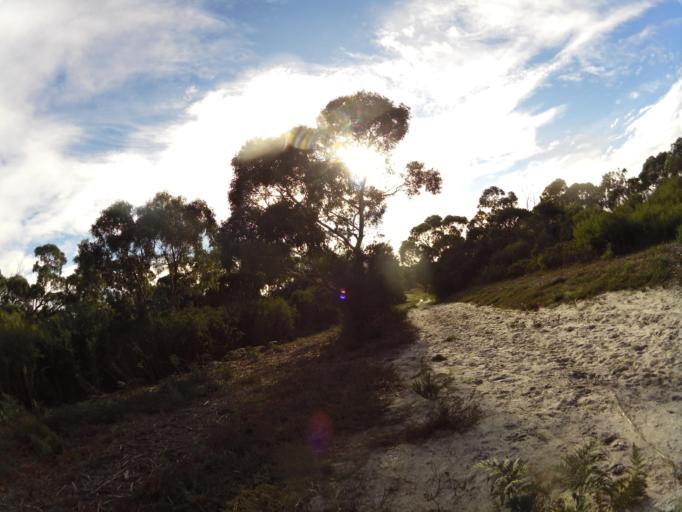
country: AU
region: Victoria
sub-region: Bass Coast
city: North Wonthaggi
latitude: -38.6302
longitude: 145.5710
